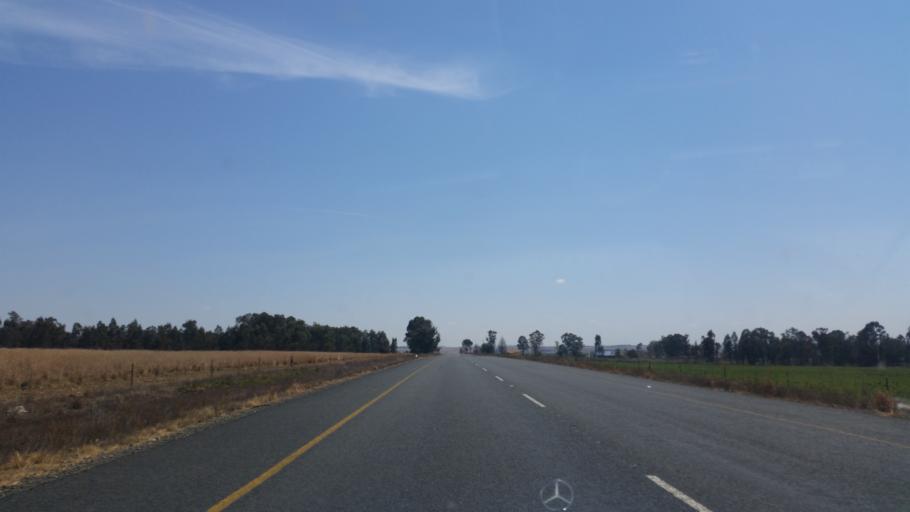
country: ZA
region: Orange Free State
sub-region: Thabo Mofutsanyana District Municipality
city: Phuthaditjhaba
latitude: -28.2153
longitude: 28.6958
